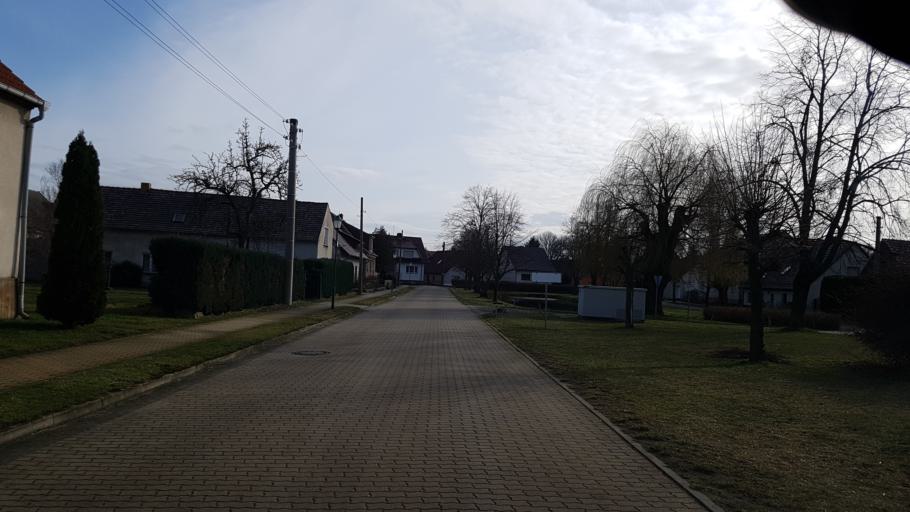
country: DE
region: Brandenburg
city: Schlieben
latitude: 51.7257
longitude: 13.3229
